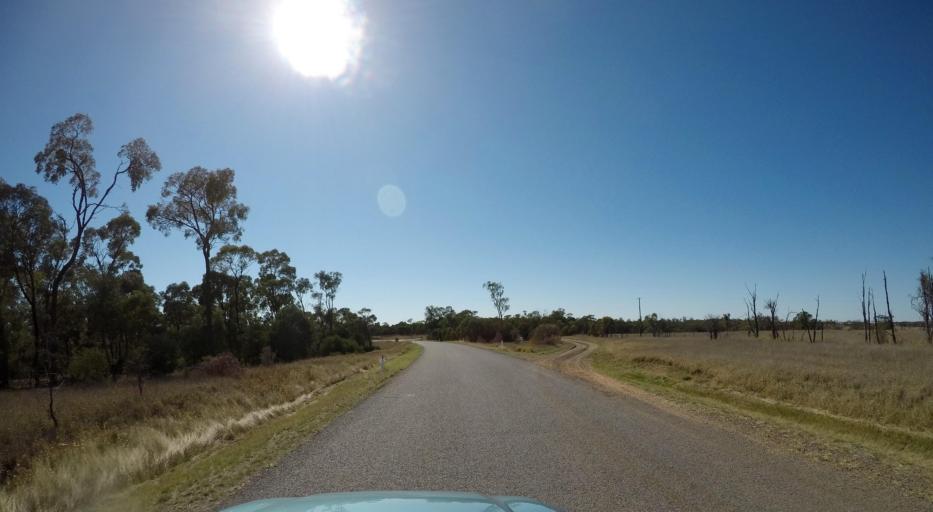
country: AU
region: Queensland
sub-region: Banana
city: Taroom
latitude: -25.7885
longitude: 149.6925
